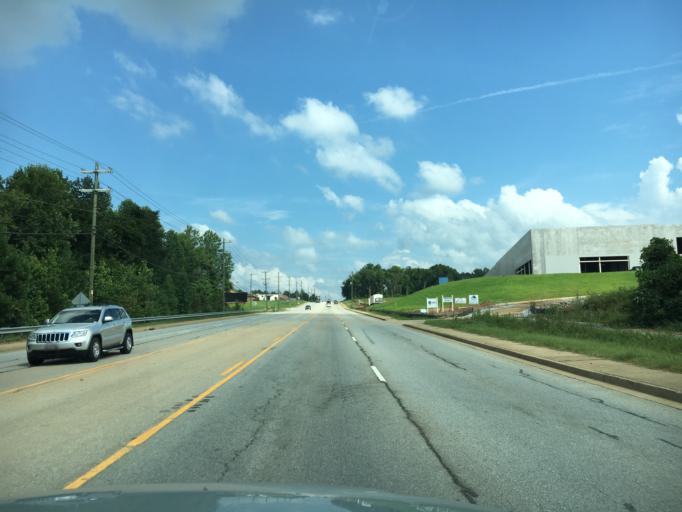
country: US
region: South Carolina
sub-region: Cherokee County
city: Gaffney
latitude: 35.0695
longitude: -81.6752
